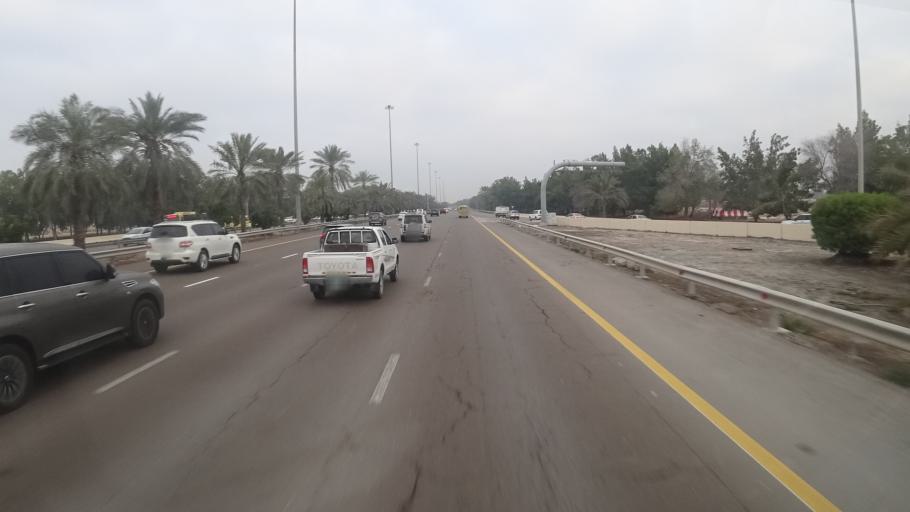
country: AE
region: Abu Dhabi
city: Abu Dhabi
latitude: 24.3550
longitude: 54.5680
